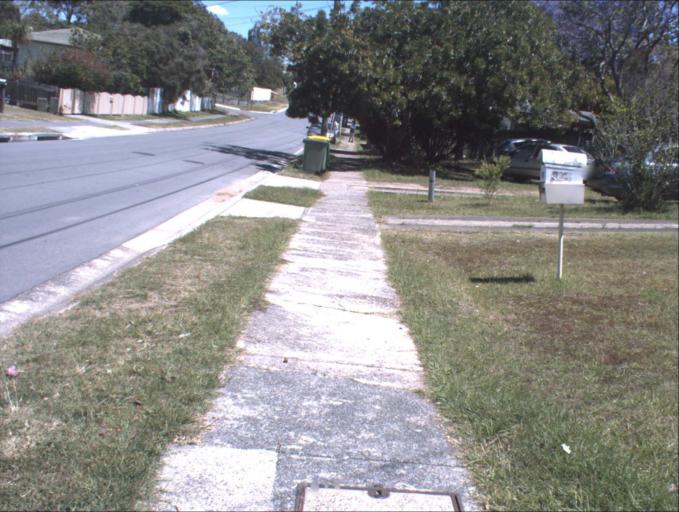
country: AU
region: Queensland
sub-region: Logan
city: Logan City
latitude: -27.6314
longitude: 153.1085
